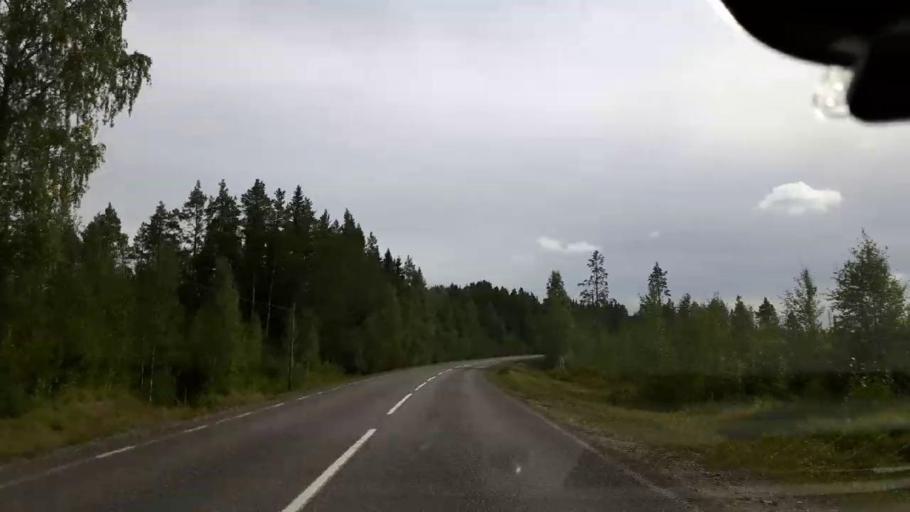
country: SE
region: Jaemtland
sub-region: Ragunda Kommun
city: Hammarstrand
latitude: 63.1442
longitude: 15.8559
